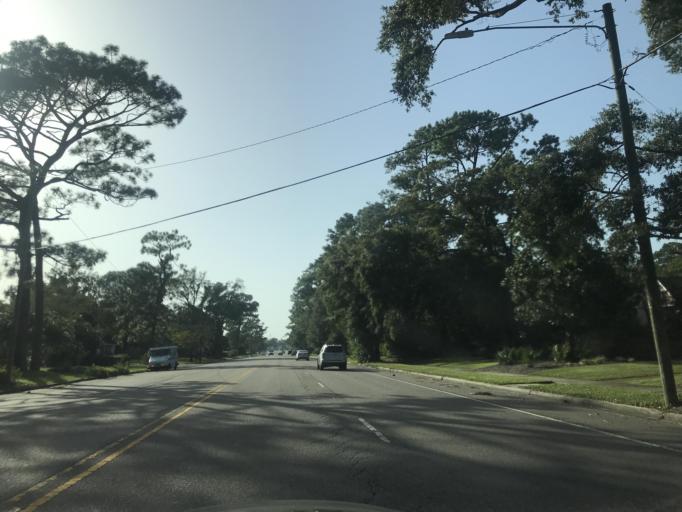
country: US
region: North Carolina
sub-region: New Hanover County
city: Wilmington
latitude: 34.2221
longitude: -77.9171
